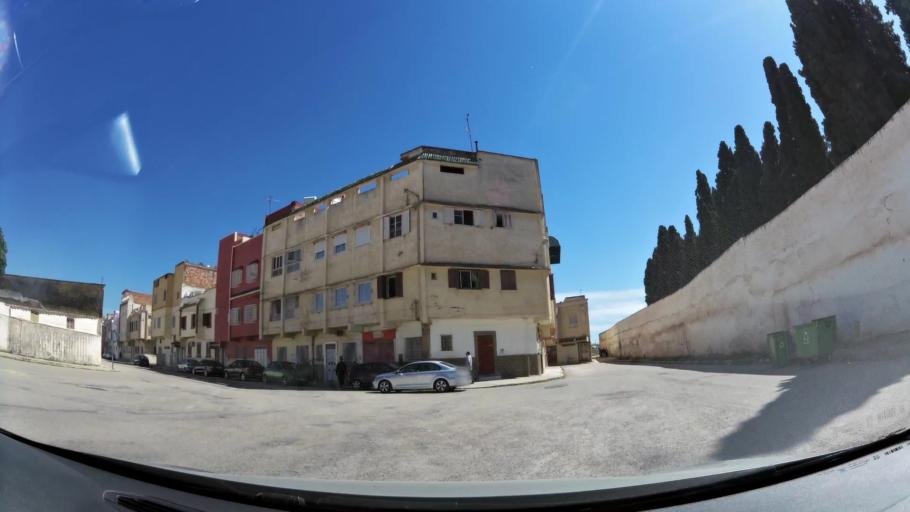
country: MA
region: Meknes-Tafilalet
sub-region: Meknes
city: Meknes
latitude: 33.8877
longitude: -5.5736
